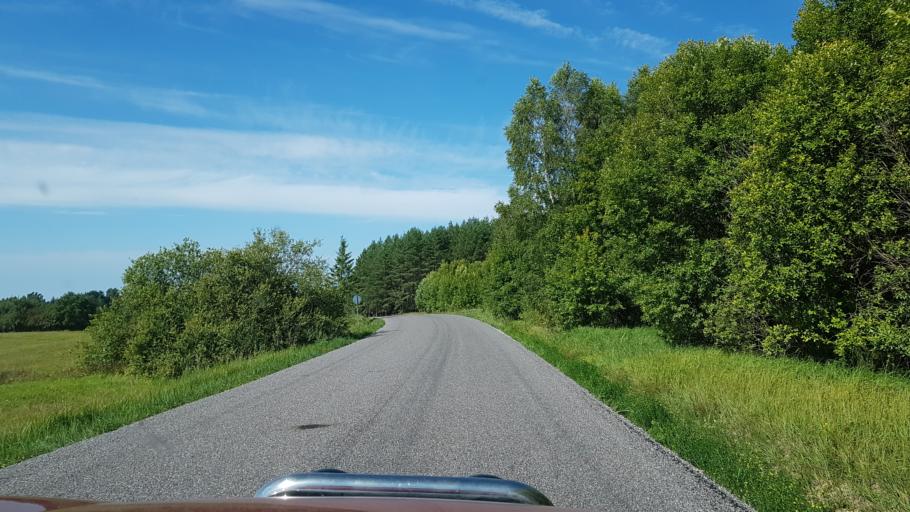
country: EE
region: Tartu
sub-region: Elva linn
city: Elva
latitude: 58.2444
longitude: 26.3937
